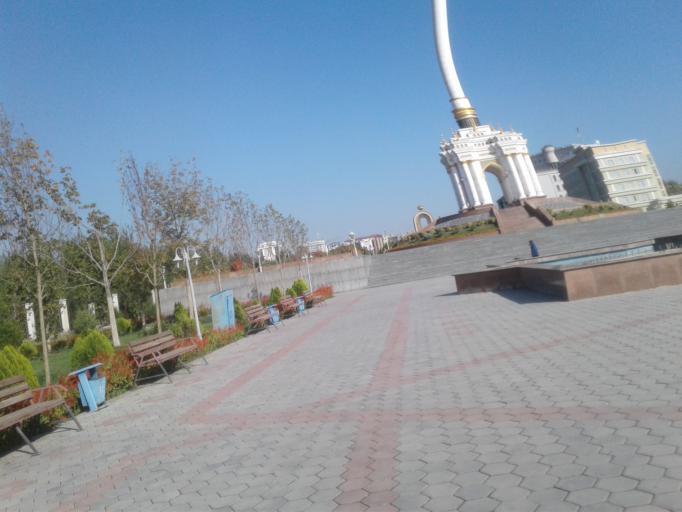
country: TJ
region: Dushanbe
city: Dushanbe
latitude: 38.5741
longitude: 68.7792
